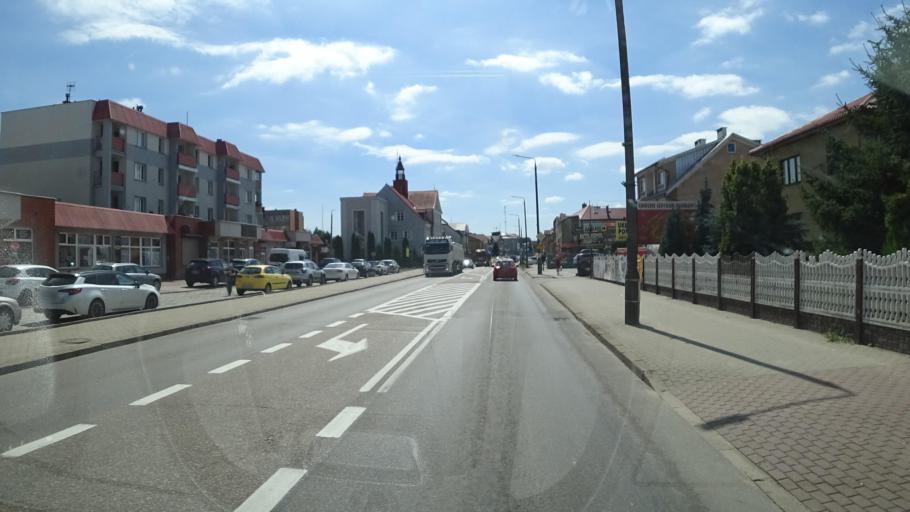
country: PL
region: Podlasie
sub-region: Powiat grajewski
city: Grajewo
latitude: 53.6505
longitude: 22.4551
